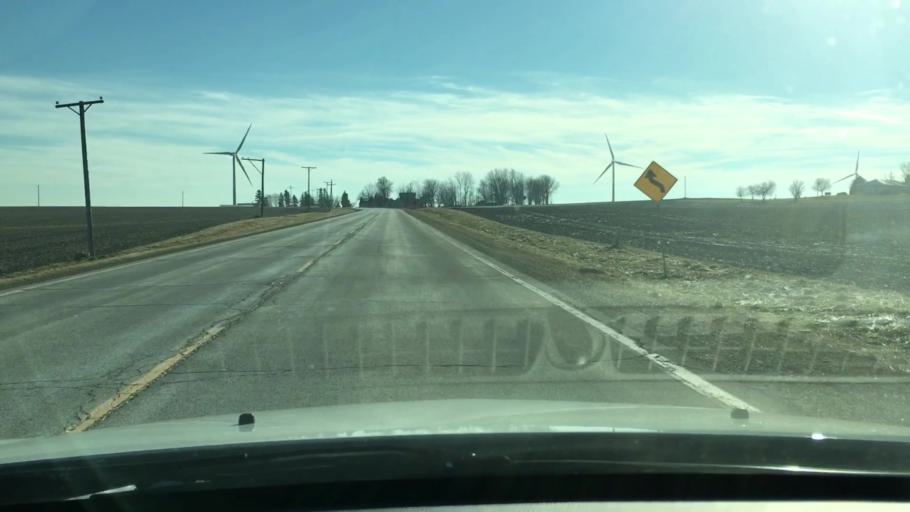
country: US
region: Illinois
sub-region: LaSalle County
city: Mendota
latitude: 41.6310
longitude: -89.1295
